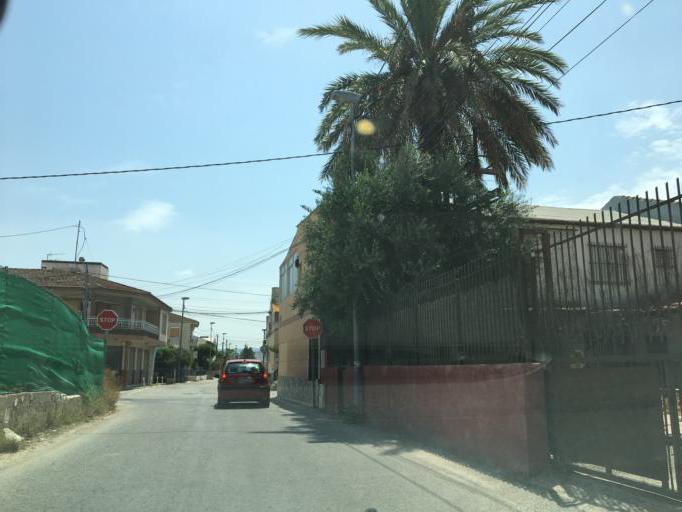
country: ES
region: Murcia
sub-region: Murcia
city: Santomera
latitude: 38.0283
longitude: -1.0494
